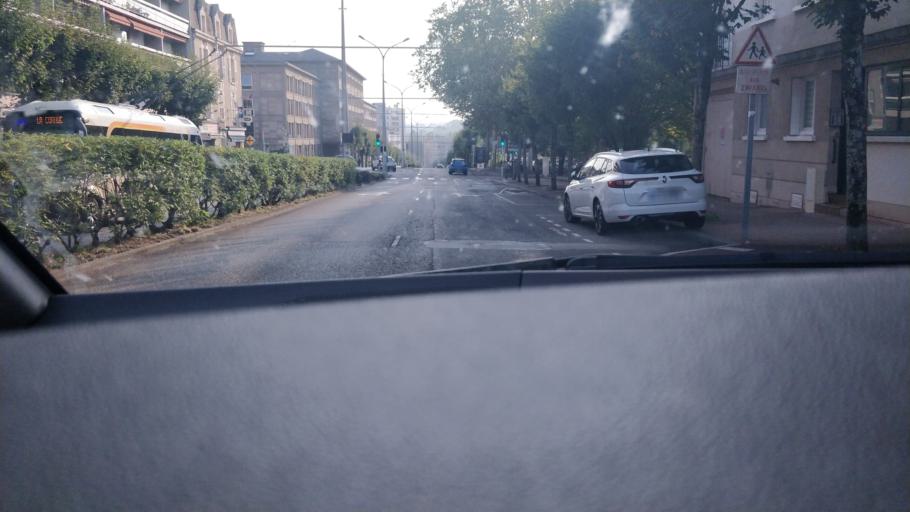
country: FR
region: Limousin
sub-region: Departement de la Haute-Vienne
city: Limoges
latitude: 45.8330
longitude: 1.2679
